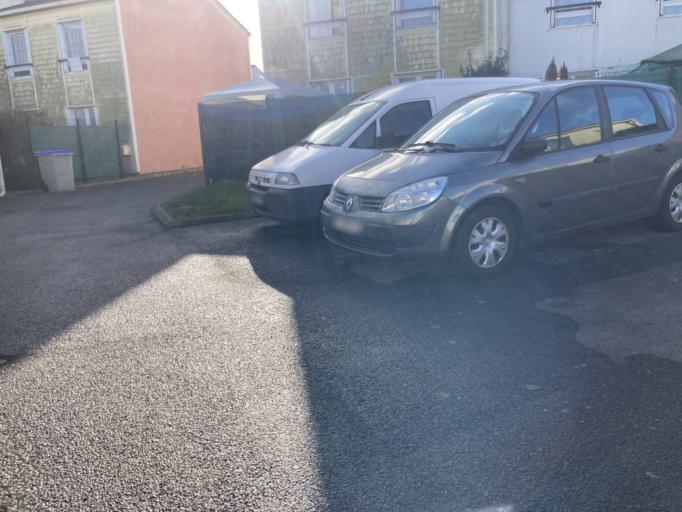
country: FR
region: Pays de la Loire
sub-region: Departement de la Loire-Atlantique
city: Saint-Sebastien-sur-Loire
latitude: 47.2072
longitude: -1.4890
